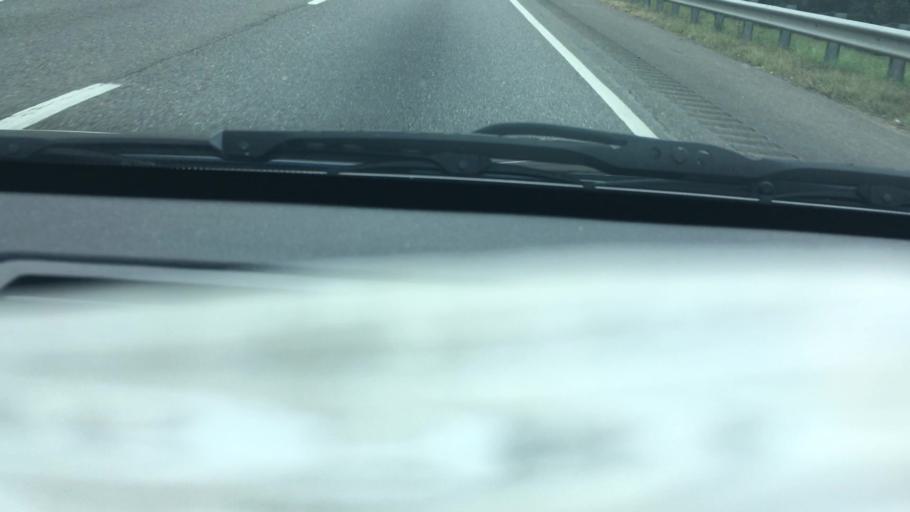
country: US
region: Alabama
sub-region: Pickens County
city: Gordo
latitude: 33.2765
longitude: -87.7681
